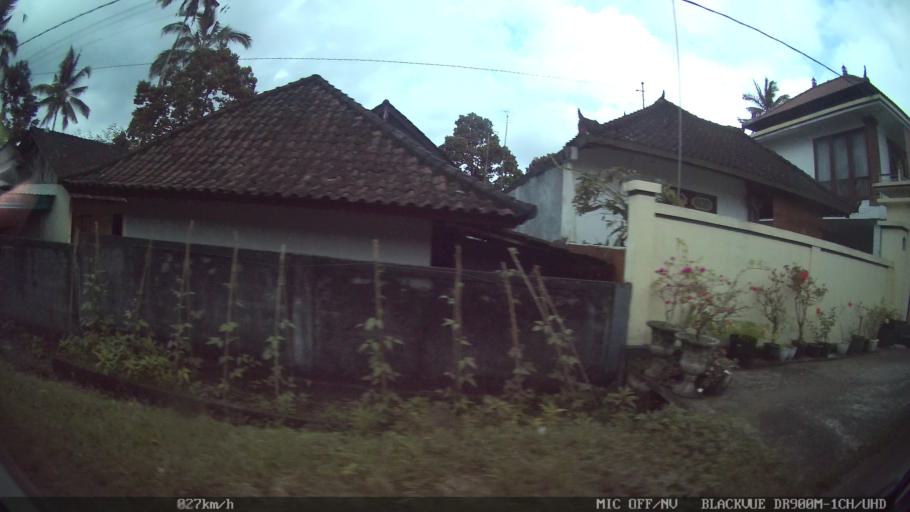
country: ID
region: Bali
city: Banjar Wangsian
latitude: -8.4553
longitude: 115.4182
